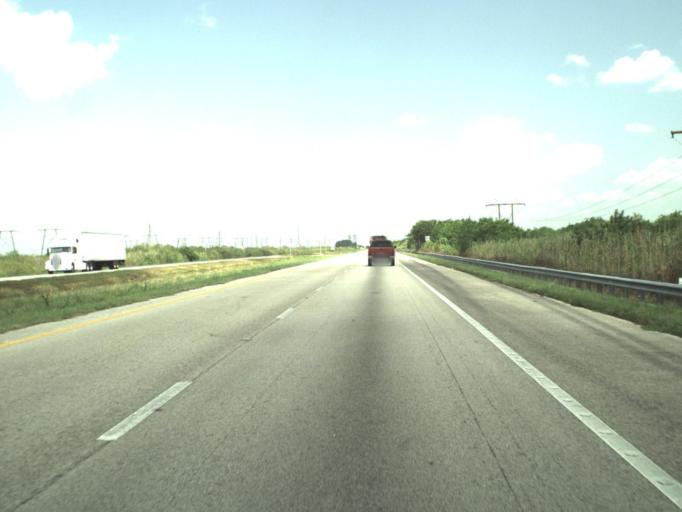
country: US
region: Florida
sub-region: Broward County
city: Weston
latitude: 26.3181
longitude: -80.5247
